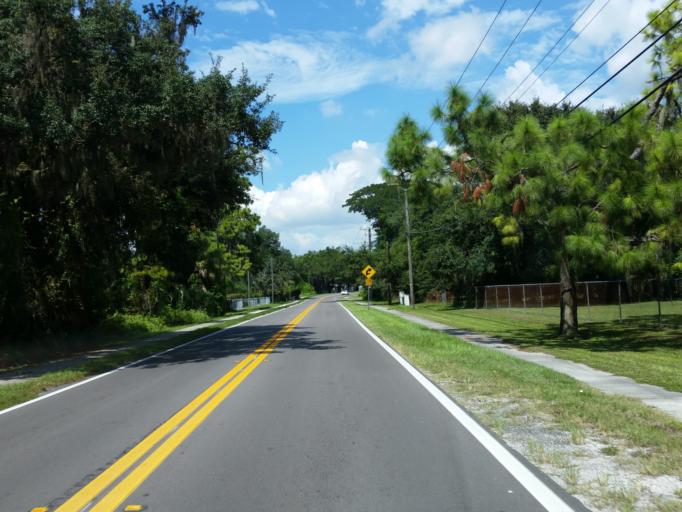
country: US
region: Florida
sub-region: Hillsborough County
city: Riverview
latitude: 27.8423
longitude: -82.3130
